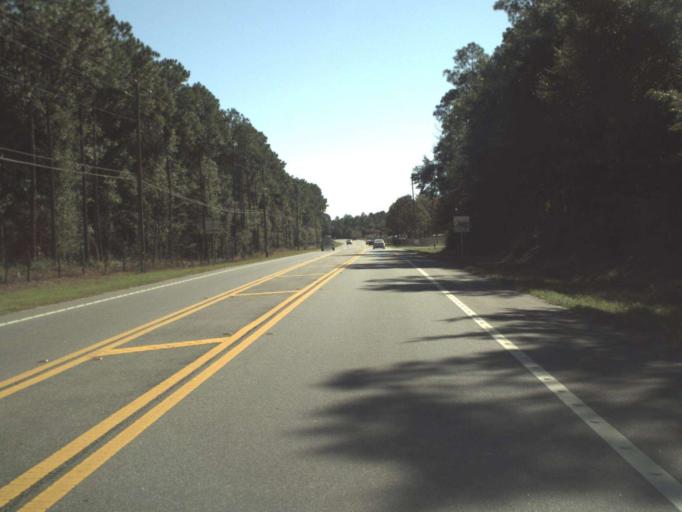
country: US
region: Florida
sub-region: Okaloosa County
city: Crestview
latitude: 30.7708
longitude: -86.6725
